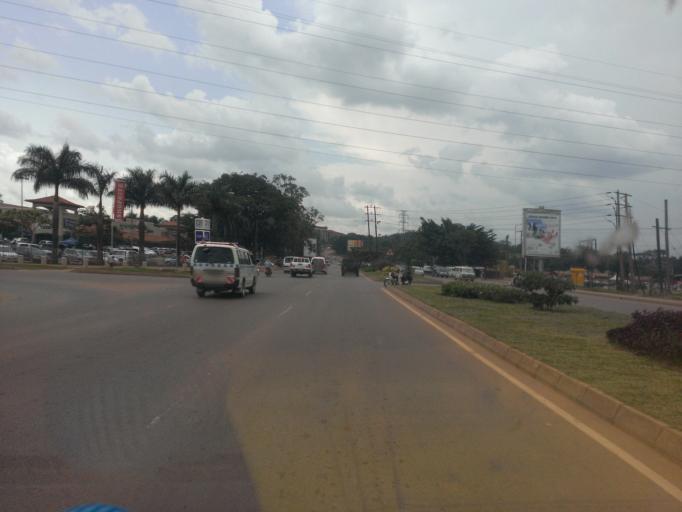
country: UG
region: Central Region
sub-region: Kampala District
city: Kampala
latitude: 0.3255
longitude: 32.6061
